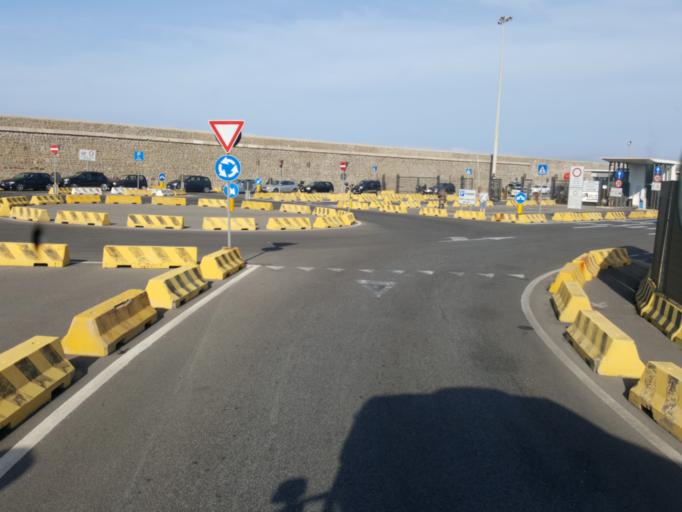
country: IT
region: Latium
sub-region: Citta metropolitana di Roma Capitale
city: Civitavecchia
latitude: 42.0891
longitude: 11.7878
